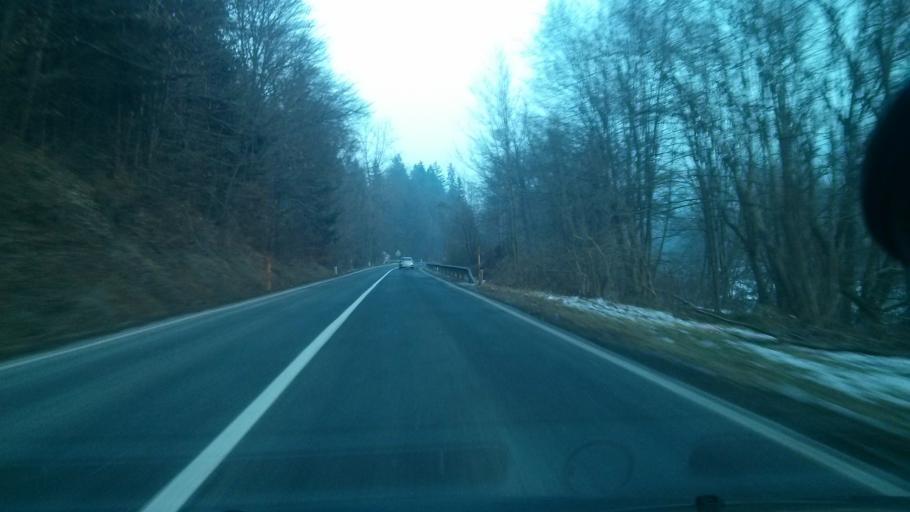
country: SI
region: Moravce
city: Moravce
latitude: 46.0912
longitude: 14.6992
